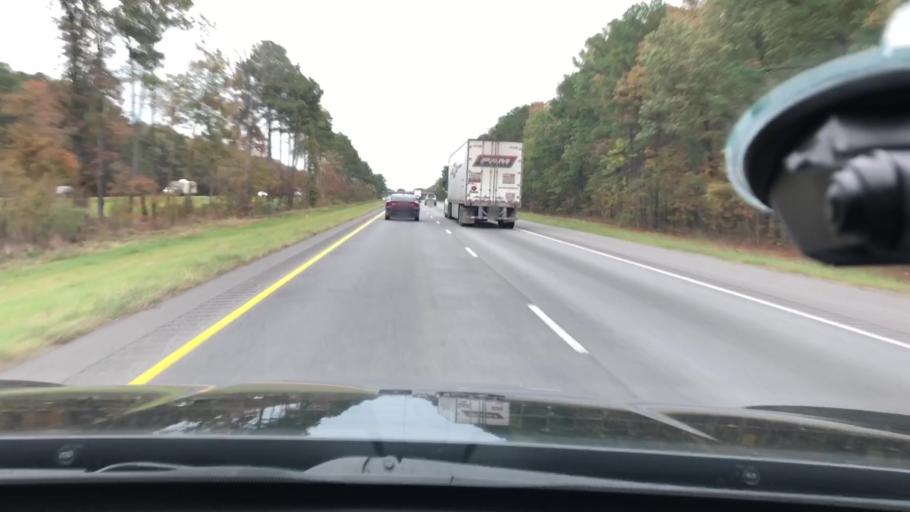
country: US
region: Arkansas
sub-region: Hempstead County
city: Hope
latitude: 33.6226
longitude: -93.7735
